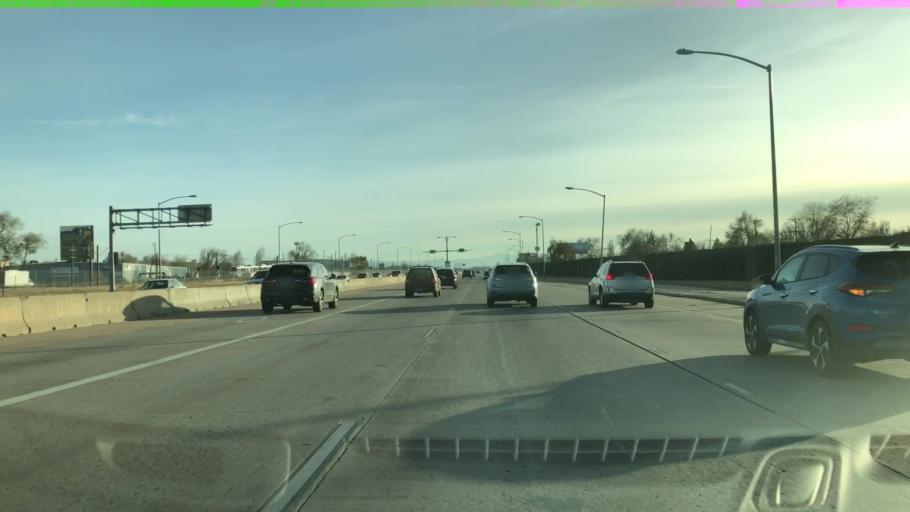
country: US
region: Colorado
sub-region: Arapahoe County
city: Englewood
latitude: 39.6750
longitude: -104.9944
